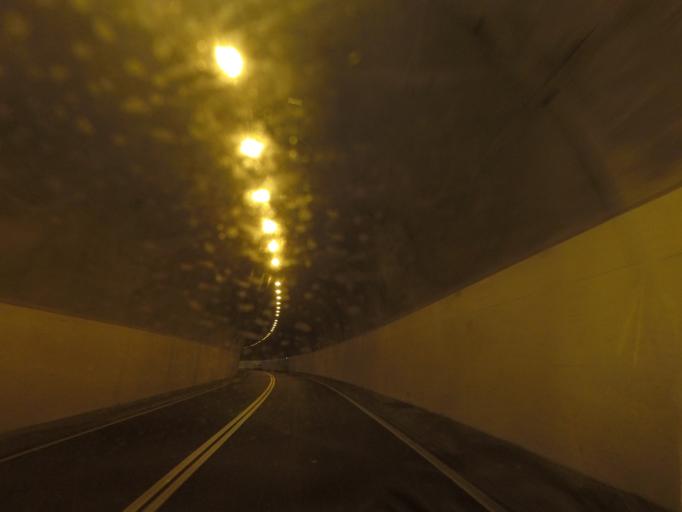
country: PT
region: Madeira
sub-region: Calheta
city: Estreito da Calheta
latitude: 32.7430
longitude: -17.1951
